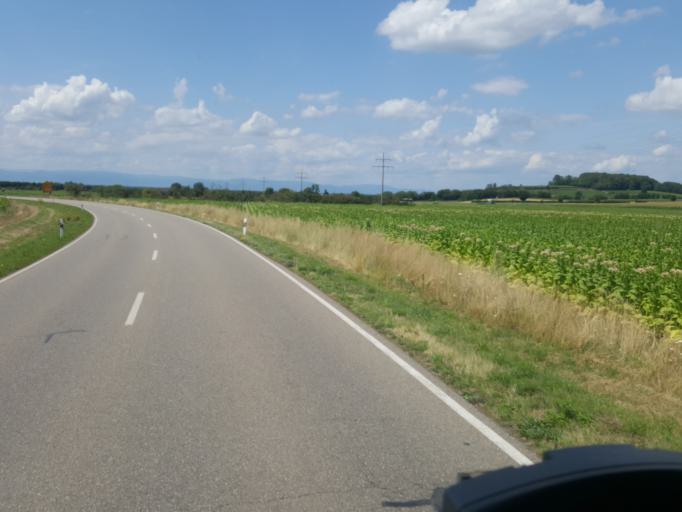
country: DE
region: Baden-Wuerttemberg
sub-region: Freiburg Region
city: Unterkrozingen
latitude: 47.9023
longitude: 7.6900
